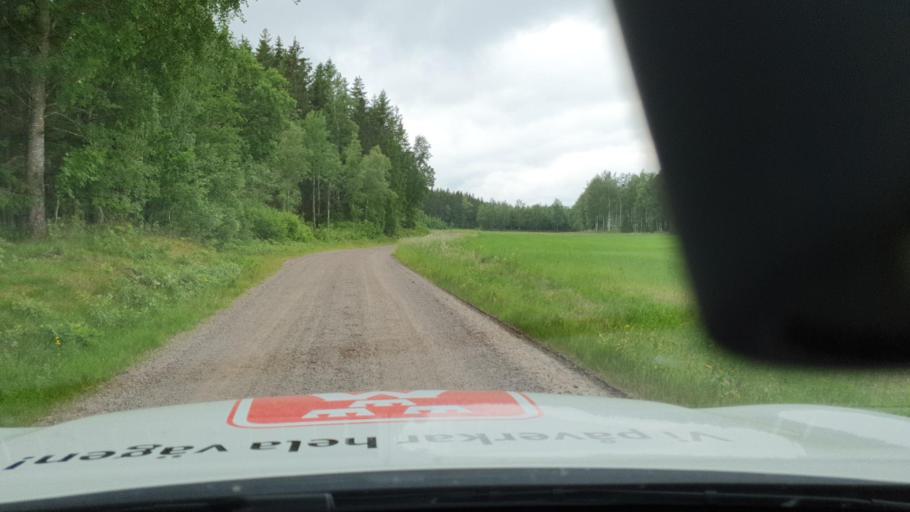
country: SE
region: Vaestra Goetaland
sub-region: Hjo Kommun
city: Hjo
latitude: 58.3488
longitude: 14.3237
